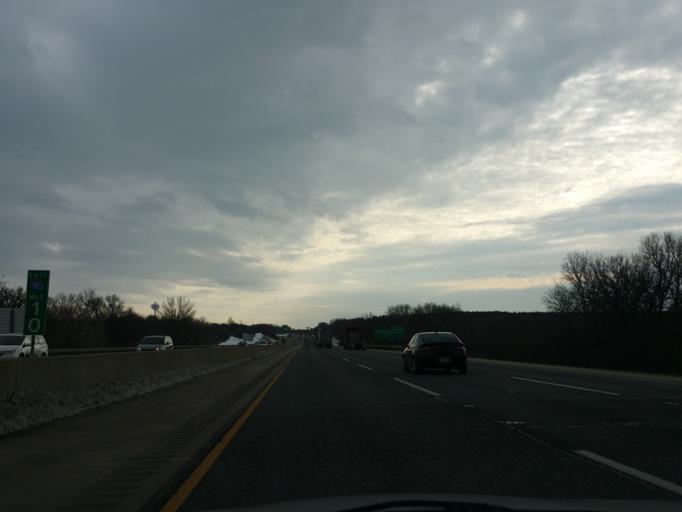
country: US
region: Illinois
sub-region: Winnebago County
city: Roscoe
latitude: 42.3549
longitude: -88.9642
